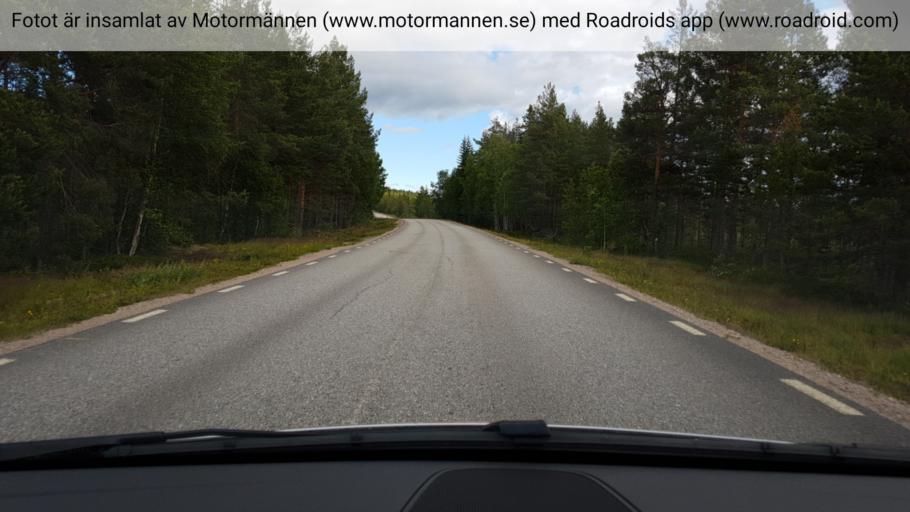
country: SE
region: Jaemtland
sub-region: Harjedalens Kommun
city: Sveg
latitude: 62.0008
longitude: 14.9216
